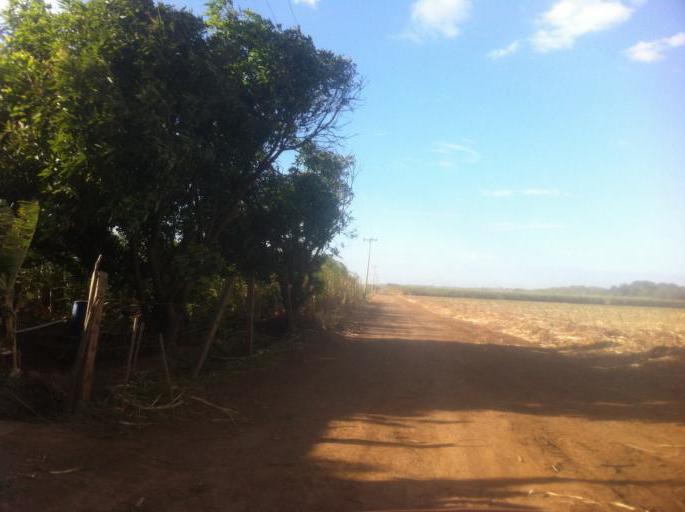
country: NI
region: Managua
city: Masachapa
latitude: 11.8593
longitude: -86.5536
